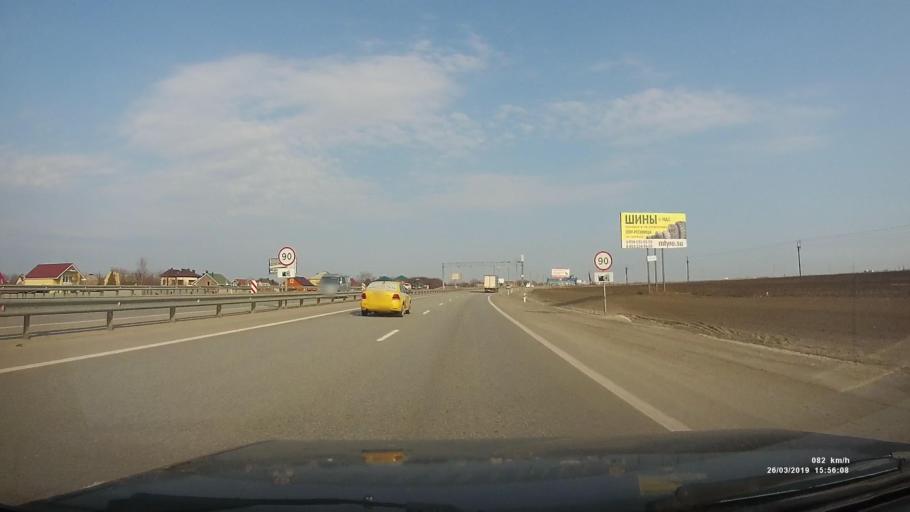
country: RU
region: Rostov
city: Krym
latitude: 47.2663
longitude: 39.5893
